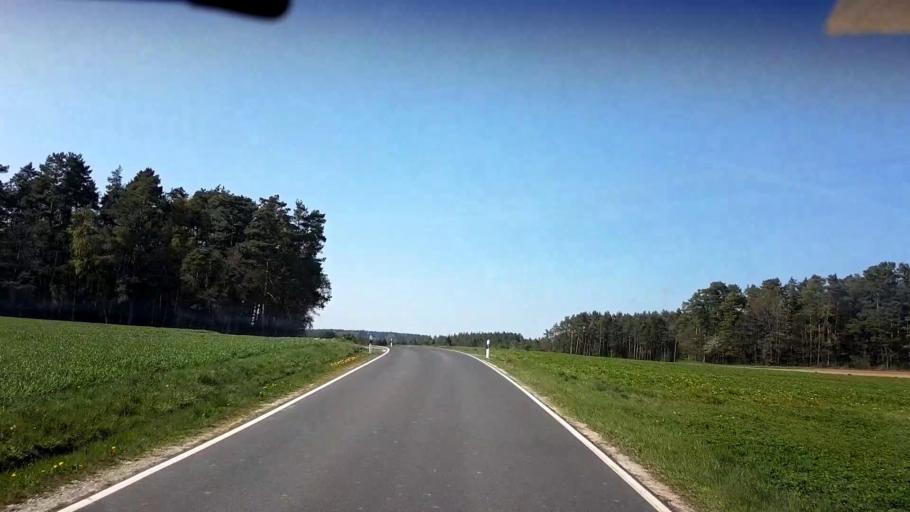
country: DE
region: Bavaria
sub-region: Upper Franconia
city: Pottenstein
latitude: 49.8024
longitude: 11.3736
